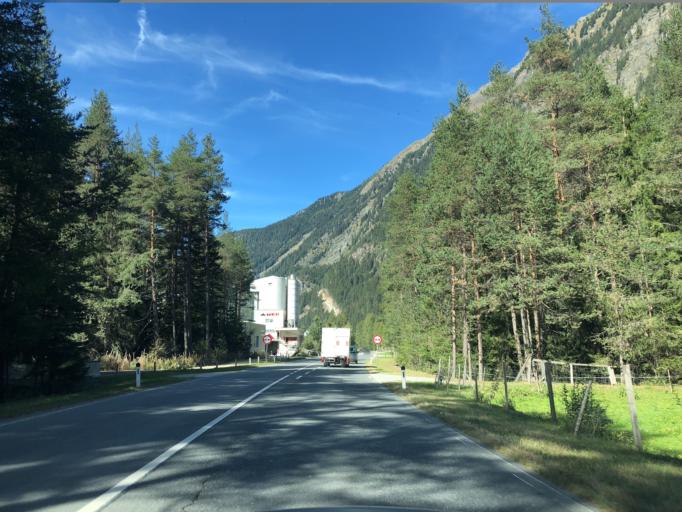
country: AT
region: Tyrol
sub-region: Politischer Bezirk Imst
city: Soelden
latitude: 47.0233
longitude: 10.9946
